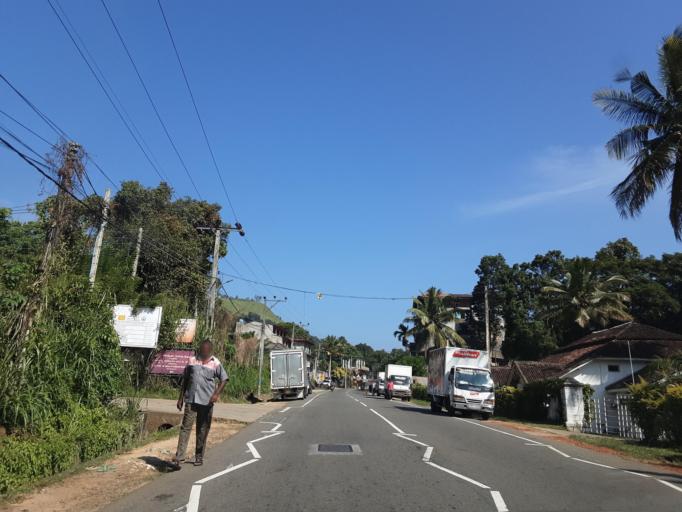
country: LK
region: Uva
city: Badulla
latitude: 6.9993
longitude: 81.0568
